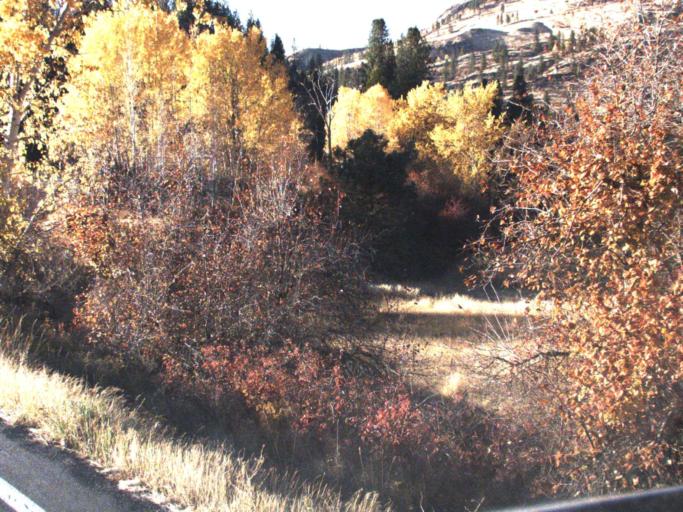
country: CA
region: British Columbia
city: Rossland
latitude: 48.8710
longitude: -117.8440
